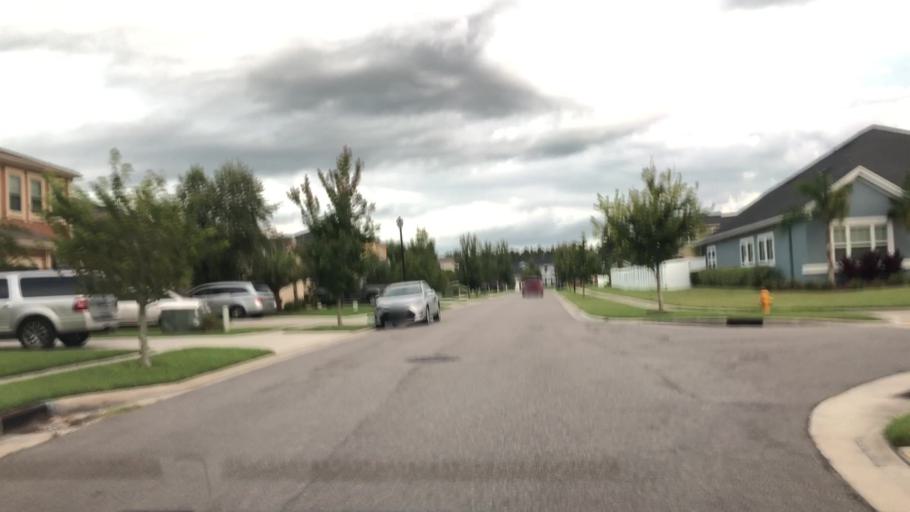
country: US
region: Florida
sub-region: Saint Johns County
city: Palm Valley
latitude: 30.0960
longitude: -81.4636
